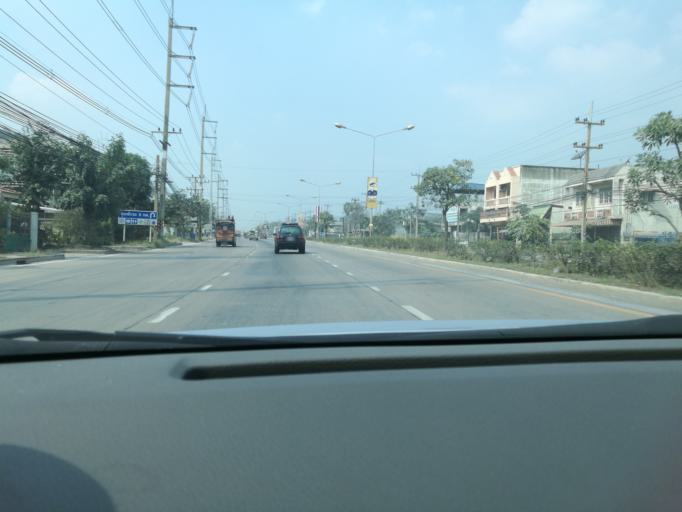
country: TH
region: Sara Buri
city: Phra Phutthabat
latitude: 14.6985
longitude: 100.8633
